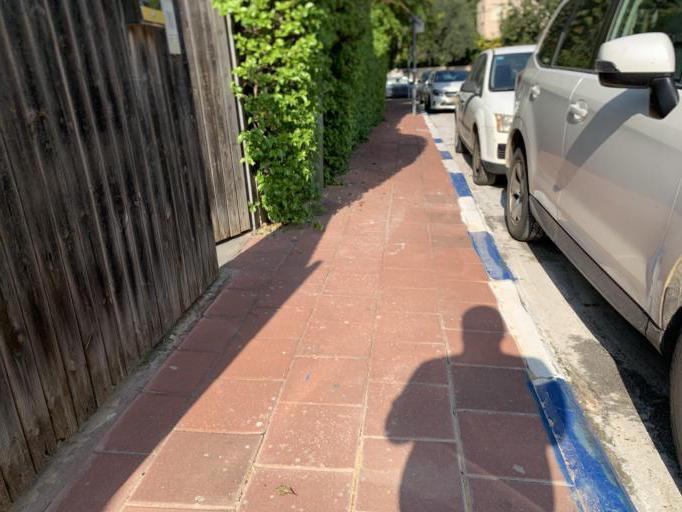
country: IL
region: Tel Aviv
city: Ramat Gan
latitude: 32.0926
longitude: 34.8129
